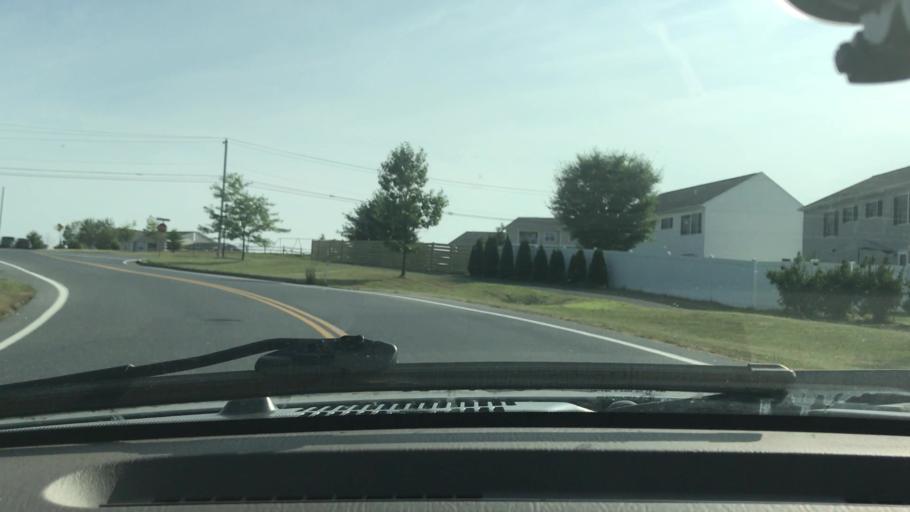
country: US
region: Pennsylvania
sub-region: Lancaster County
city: Rheems
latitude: 40.1414
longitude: -76.5669
